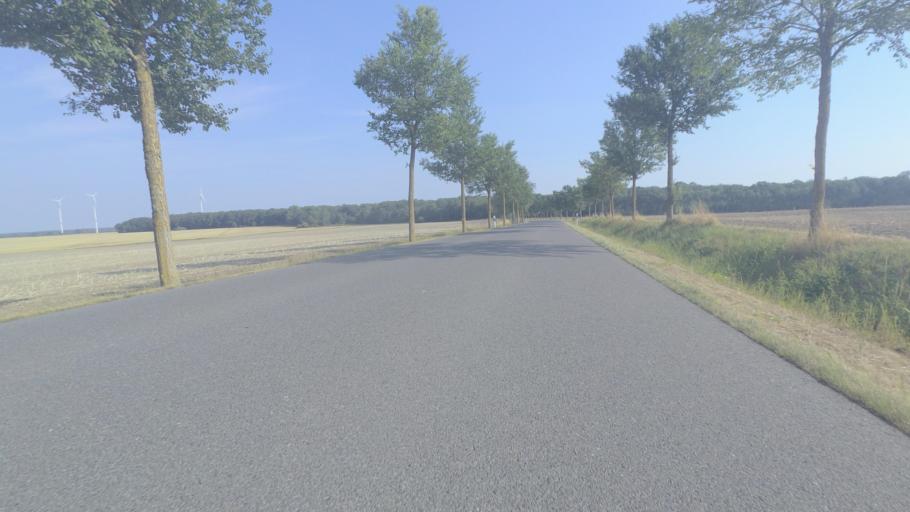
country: DE
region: Mecklenburg-Vorpommern
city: Grimmen
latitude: 54.1385
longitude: 13.0640
